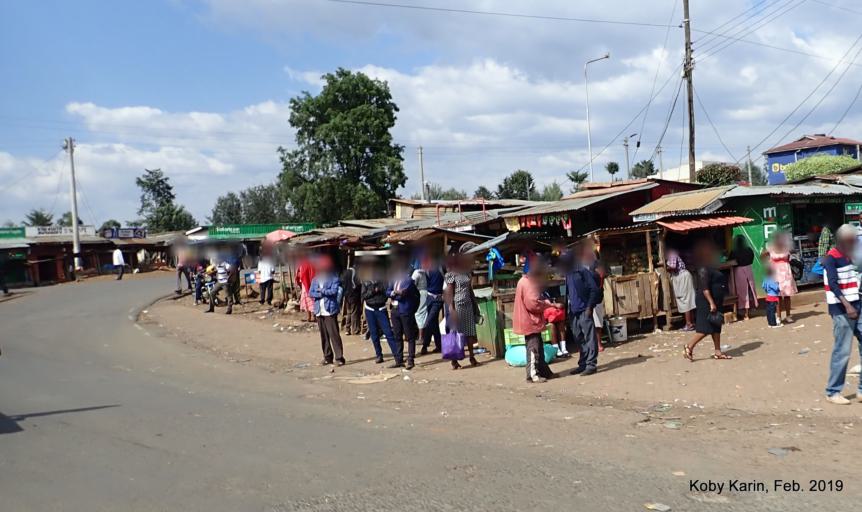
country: KE
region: Kericho
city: Sotik
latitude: -0.6769
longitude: 35.1391
